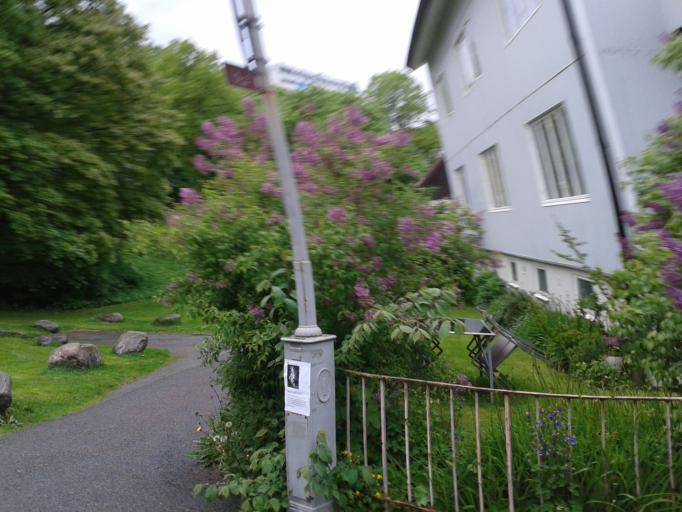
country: SE
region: Vaestra Goetaland
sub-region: Goteborg
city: Goeteborg
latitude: 57.6878
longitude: 11.9887
